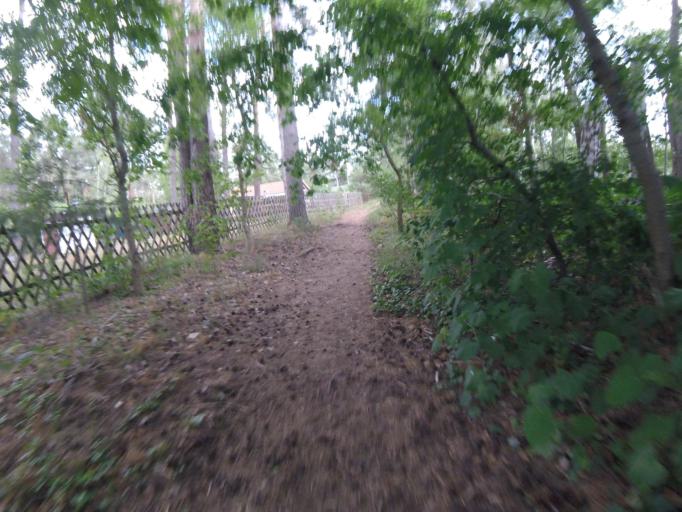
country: DE
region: Brandenburg
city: Halbe
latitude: 52.1134
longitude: 13.6916
